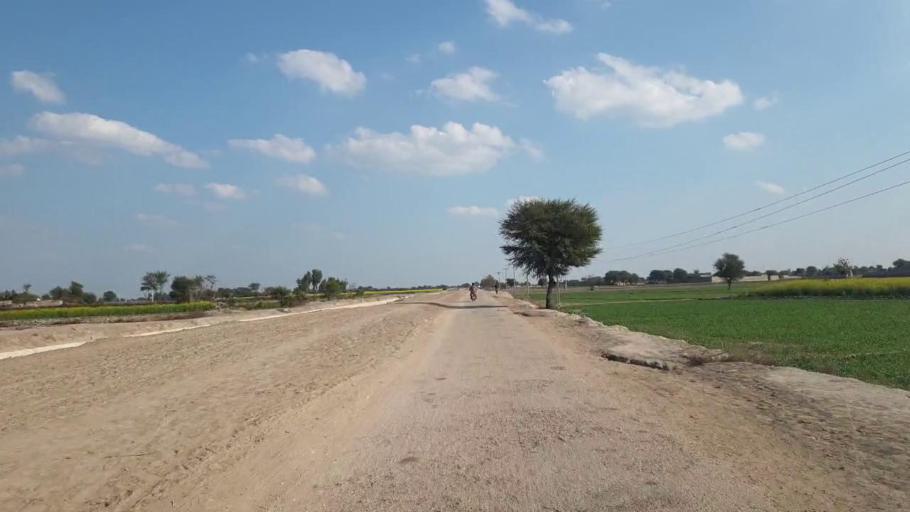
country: PK
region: Sindh
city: Shahpur Chakar
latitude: 26.1102
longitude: 68.5697
